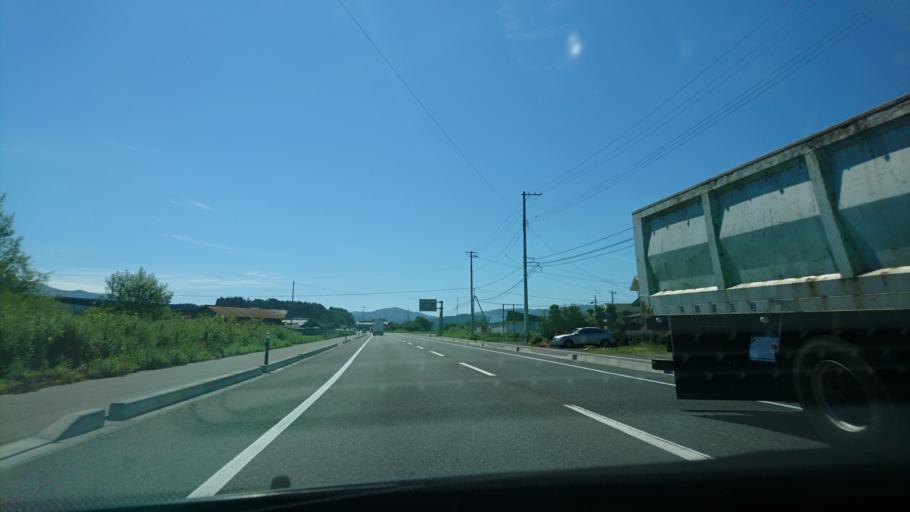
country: JP
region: Iwate
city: Tono
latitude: 39.3103
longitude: 141.5711
